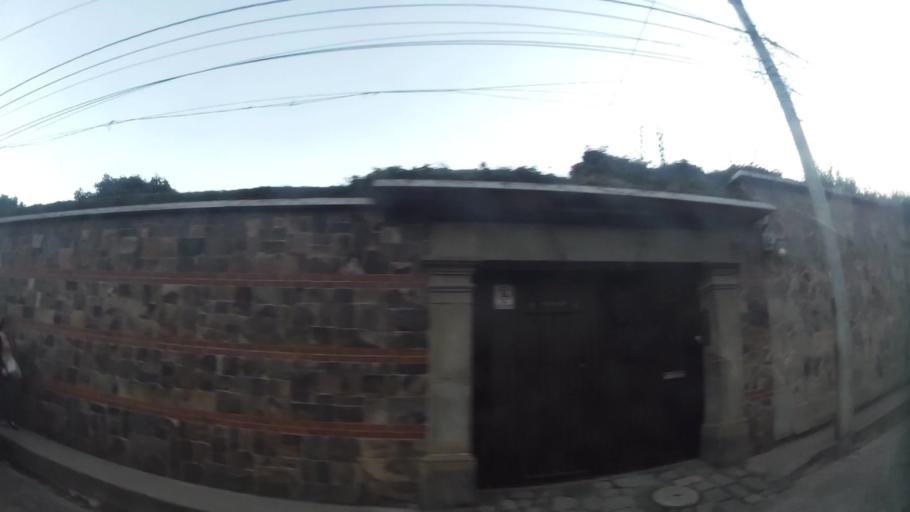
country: GT
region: Sacatepequez
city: Antigua Guatemala
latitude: 14.5603
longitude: -90.7276
